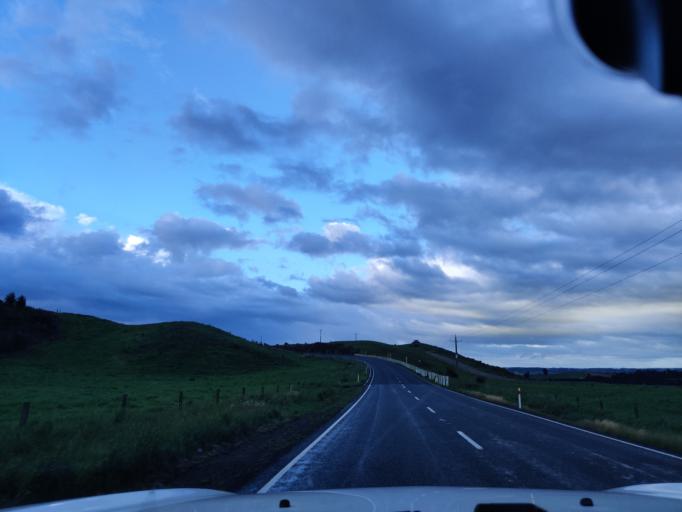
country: NZ
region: Waikato
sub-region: South Waikato District
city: Tokoroa
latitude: -38.3845
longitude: 175.7830
